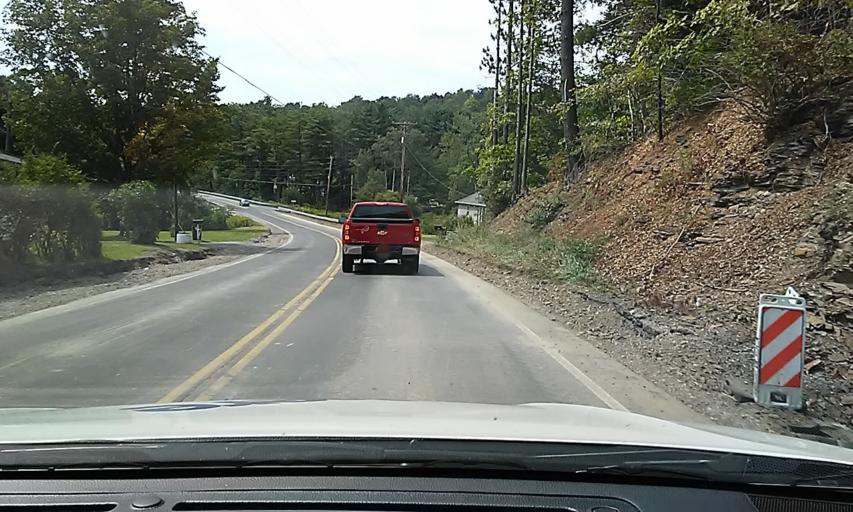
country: US
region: Pennsylvania
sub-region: Clearfield County
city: Treasure Lake
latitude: 41.1676
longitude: -78.6609
